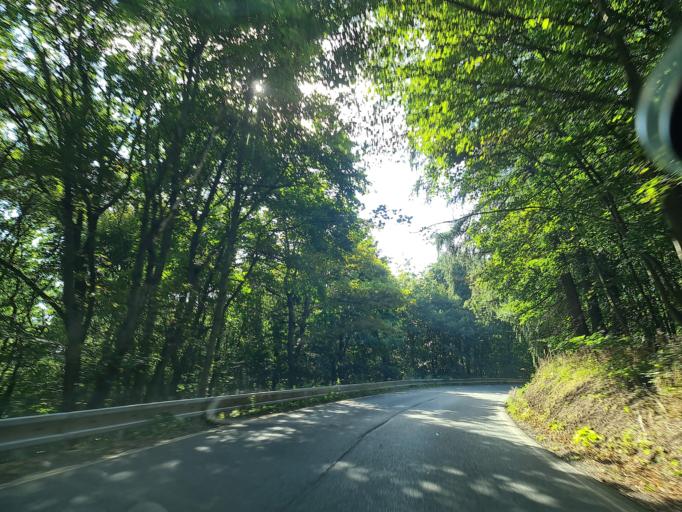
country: CZ
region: Ustecky
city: Mezibori
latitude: 50.6164
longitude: 13.5746
